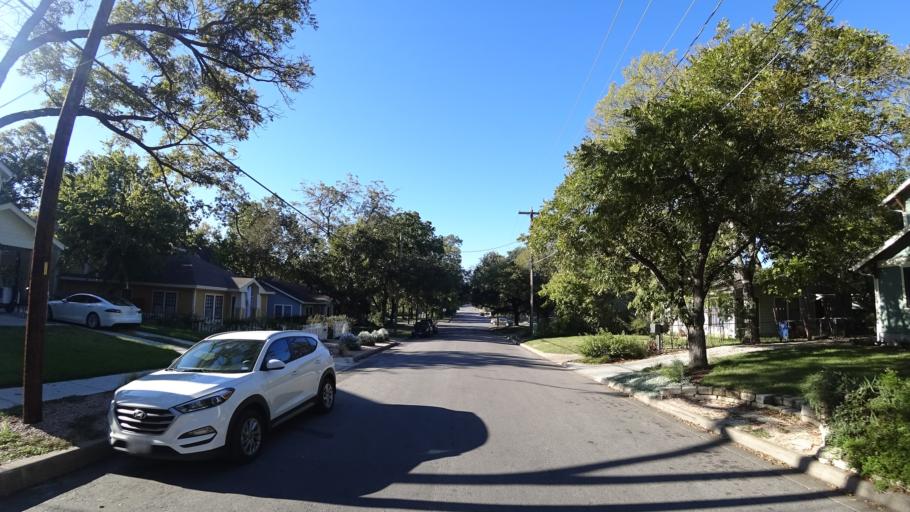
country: US
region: Texas
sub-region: Travis County
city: Austin
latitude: 30.3082
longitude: -97.7262
